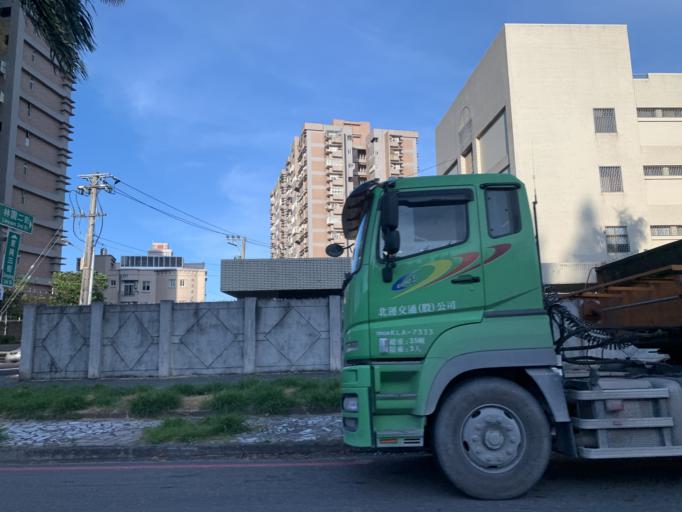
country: TW
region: Taiwan
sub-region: Hualien
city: Hualian
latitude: 24.0033
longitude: 121.6294
